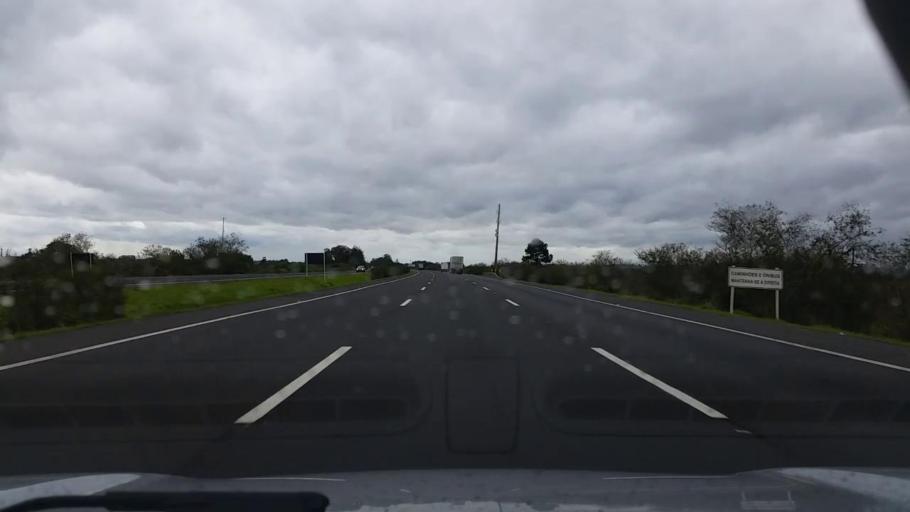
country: BR
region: Rio Grande do Sul
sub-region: Rolante
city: Rolante
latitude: -29.8862
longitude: -50.6587
